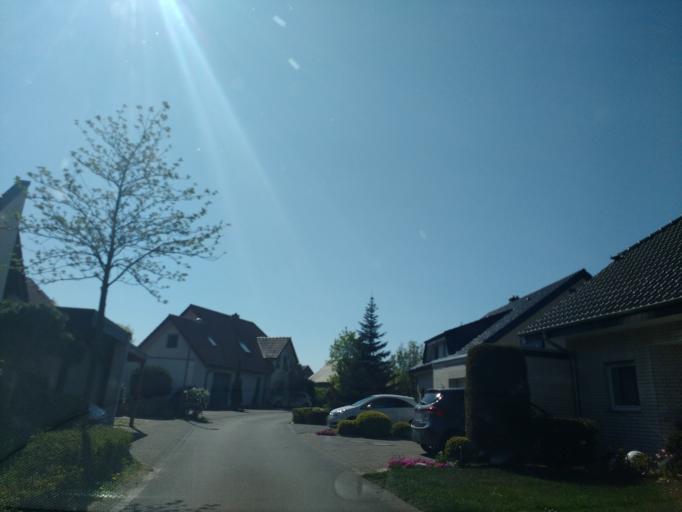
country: DE
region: North Rhine-Westphalia
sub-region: Regierungsbezirk Detmold
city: Delbruck
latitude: 51.7653
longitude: 8.5822
